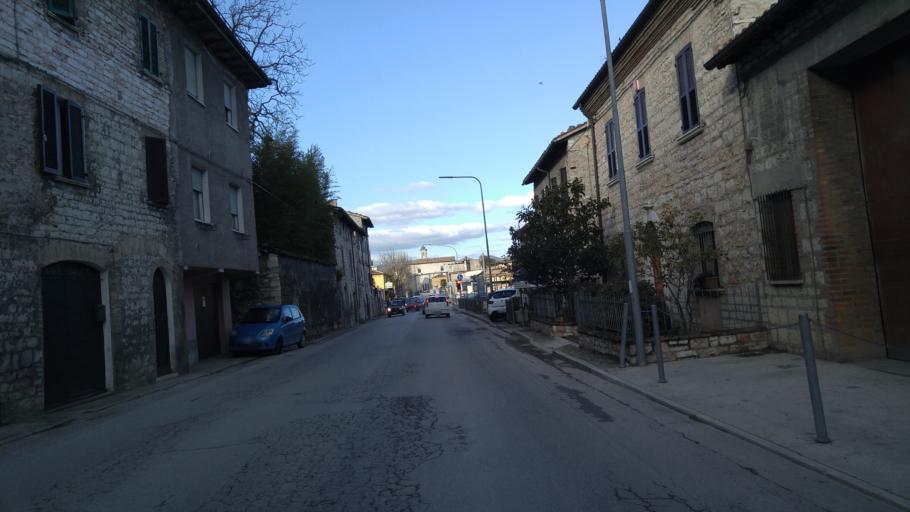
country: IT
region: The Marches
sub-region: Provincia di Pesaro e Urbino
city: Cagli
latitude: 43.5452
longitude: 12.6500
